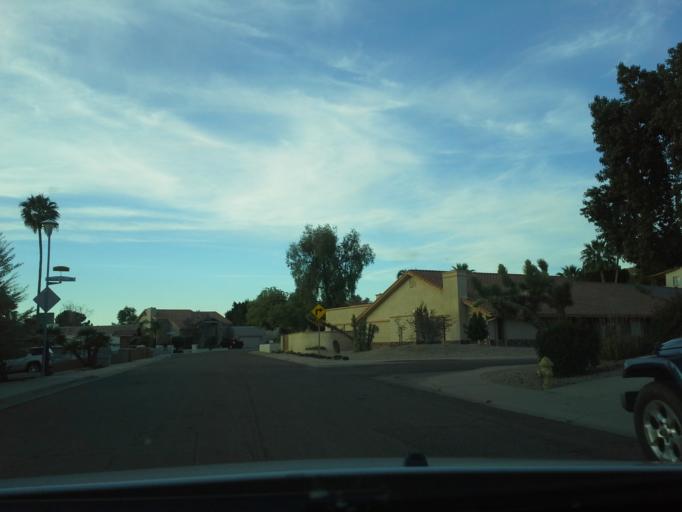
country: US
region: Arizona
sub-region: Maricopa County
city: Paradise Valley
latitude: 33.6210
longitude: -112.0606
